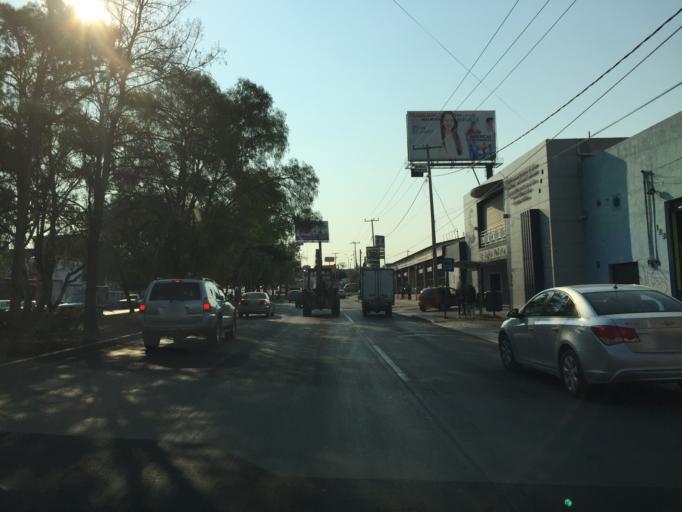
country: MX
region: Aguascalientes
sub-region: Aguascalientes
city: Aguascalientes
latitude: 21.8585
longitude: -102.3079
